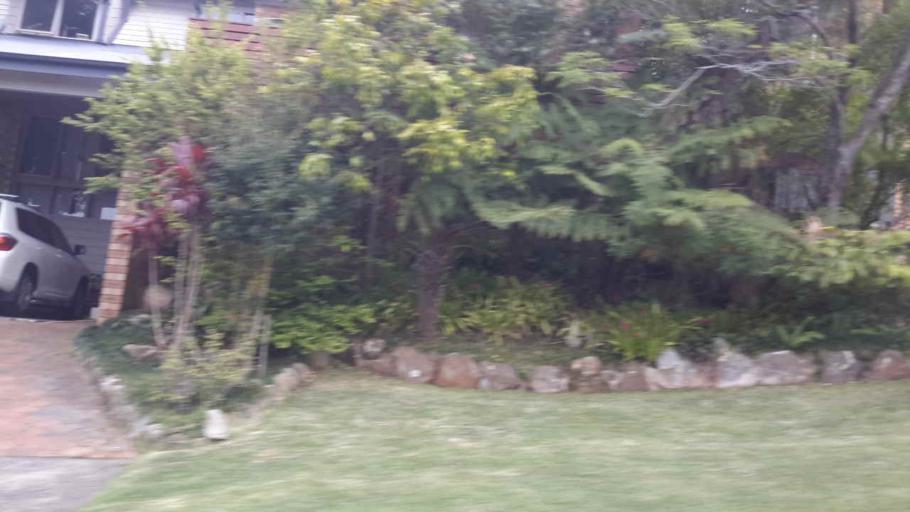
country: AU
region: New South Wales
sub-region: Wollongong
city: Bulli
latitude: -34.3133
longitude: 150.9110
